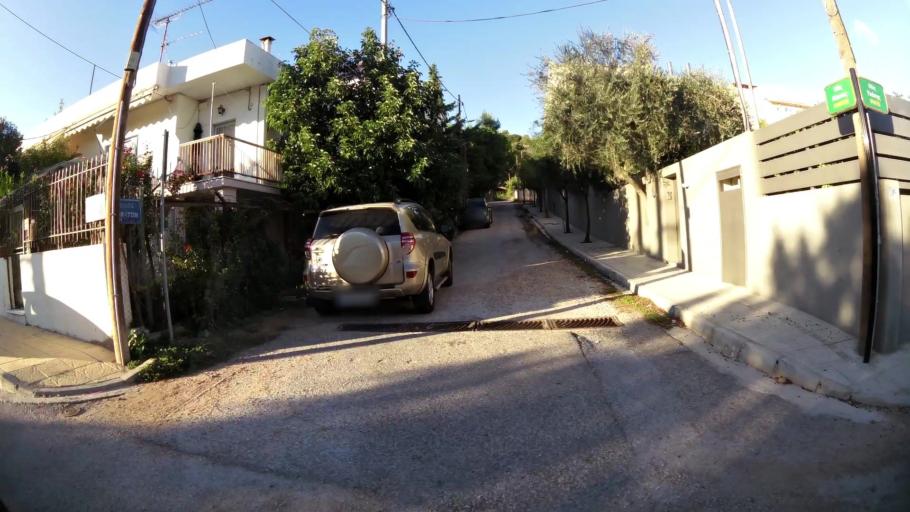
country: GR
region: Attica
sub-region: Nomarchia Anatolikis Attikis
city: Vari
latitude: 37.8276
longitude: 23.7982
